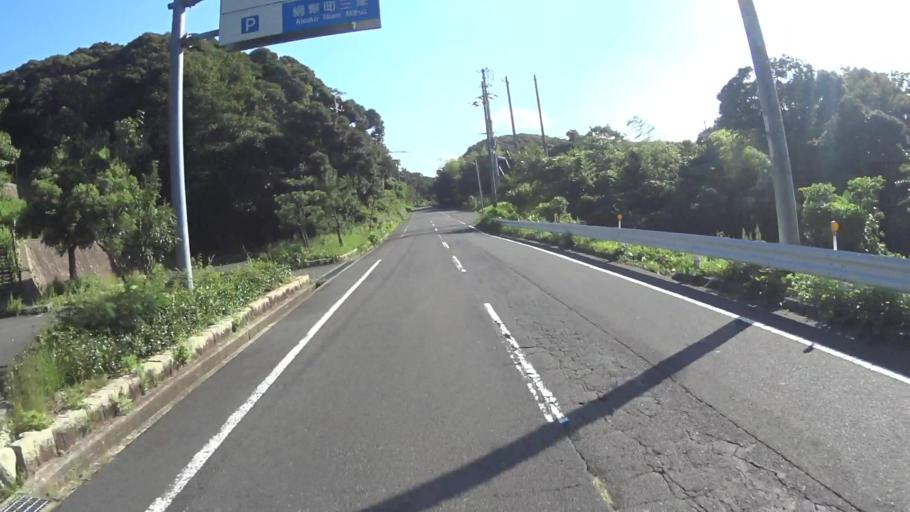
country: JP
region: Kyoto
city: Miyazu
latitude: 35.7068
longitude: 135.0693
